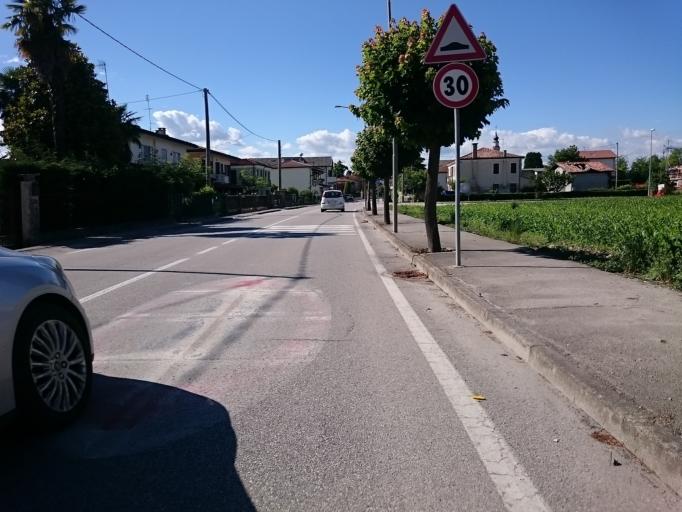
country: IT
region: Veneto
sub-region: Provincia di Padova
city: Saonara
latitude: 45.3663
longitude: 11.9864
